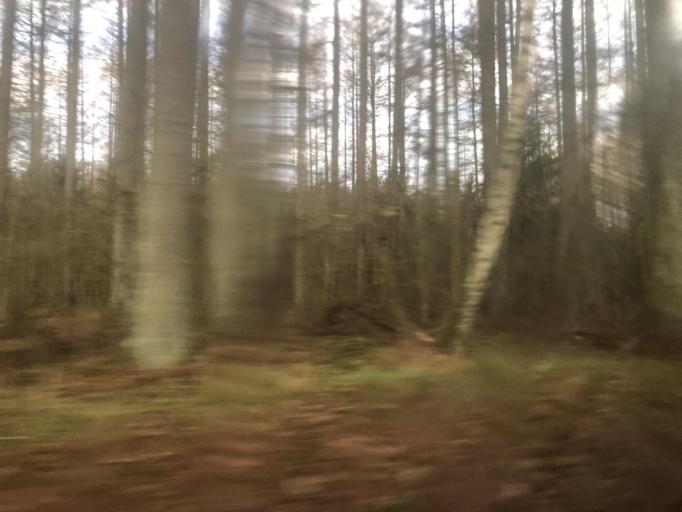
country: SE
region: Skane
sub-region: Lunds Kommun
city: Veberod
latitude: 55.6070
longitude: 13.5378
